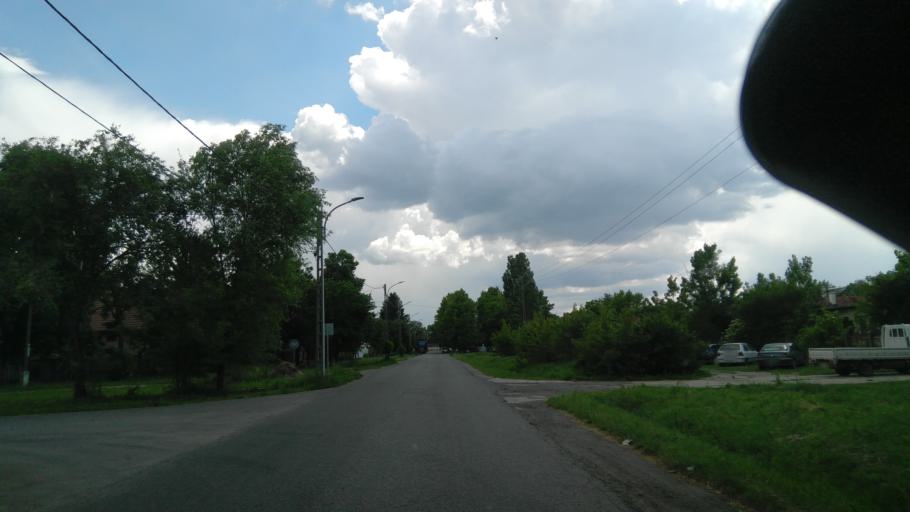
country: HU
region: Bekes
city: Gyula
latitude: 46.6611
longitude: 21.2696
